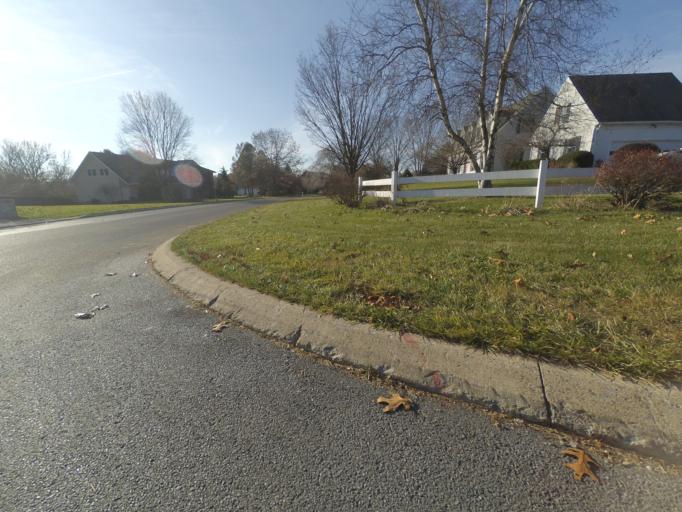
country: US
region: Pennsylvania
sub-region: Centre County
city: Lemont
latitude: 40.7921
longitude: -77.8270
